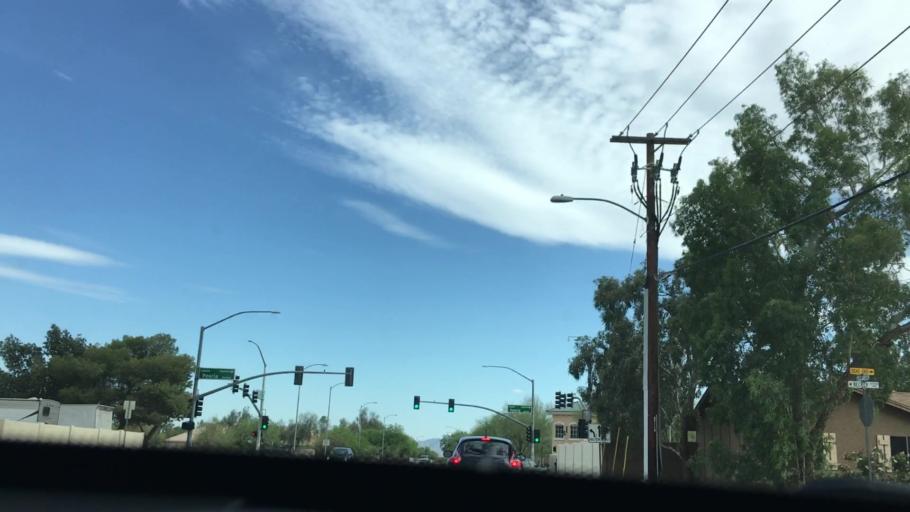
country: US
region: Arizona
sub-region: Maricopa County
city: Peoria
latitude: 33.5818
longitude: -112.2291
